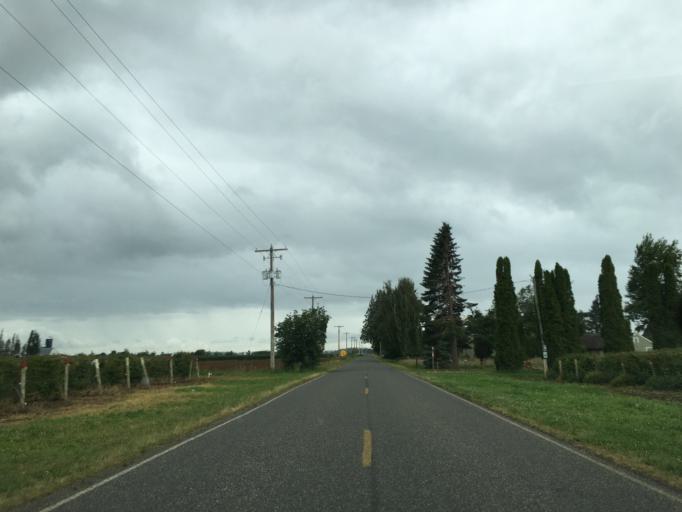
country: US
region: Washington
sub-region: Whatcom County
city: Lynden
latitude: 48.9787
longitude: -122.4149
